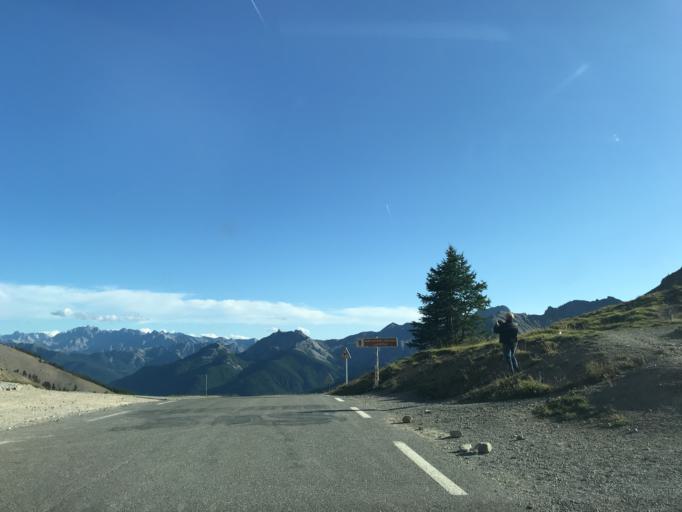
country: IT
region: Piedmont
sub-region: Provincia di Torino
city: Claviere
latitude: 44.8197
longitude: 6.7350
